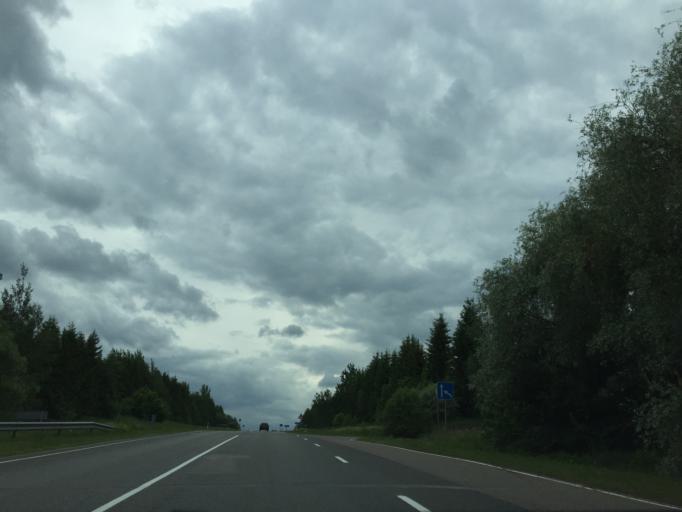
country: LV
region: Apes Novads
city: Ape
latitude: 57.4547
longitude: 26.3442
